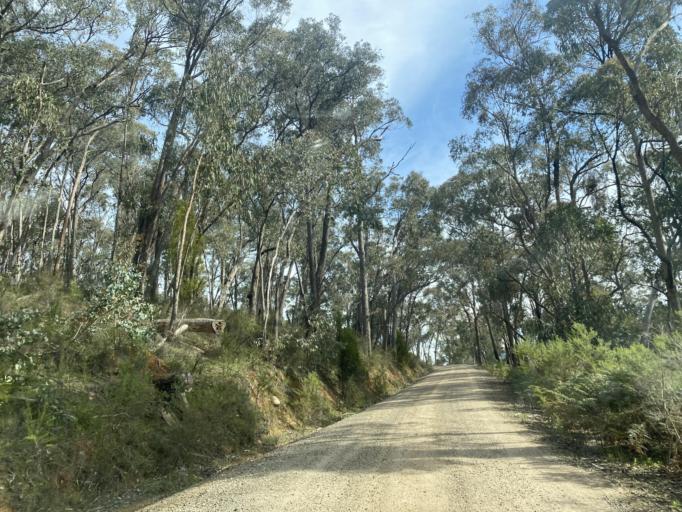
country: AU
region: Victoria
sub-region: Mansfield
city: Mansfield
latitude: -36.8305
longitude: 146.1648
